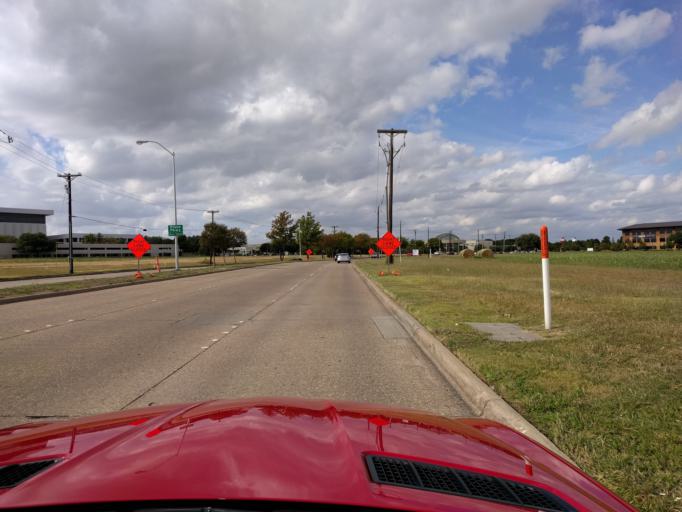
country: US
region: Texas
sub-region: Collin County
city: Plano
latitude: 33.0047
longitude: -96.7327
